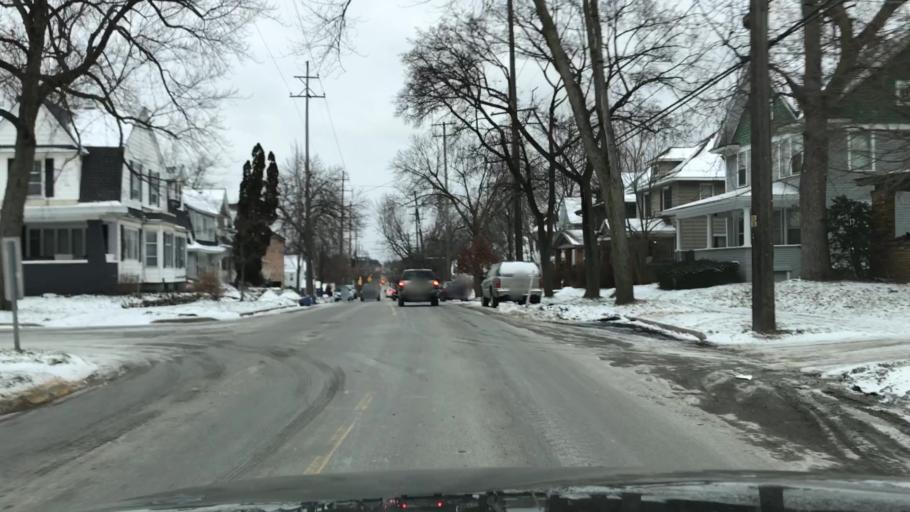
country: US
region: Michigan
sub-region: Kent County
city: Grand Rapids
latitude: 42.9608
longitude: -85.6397
